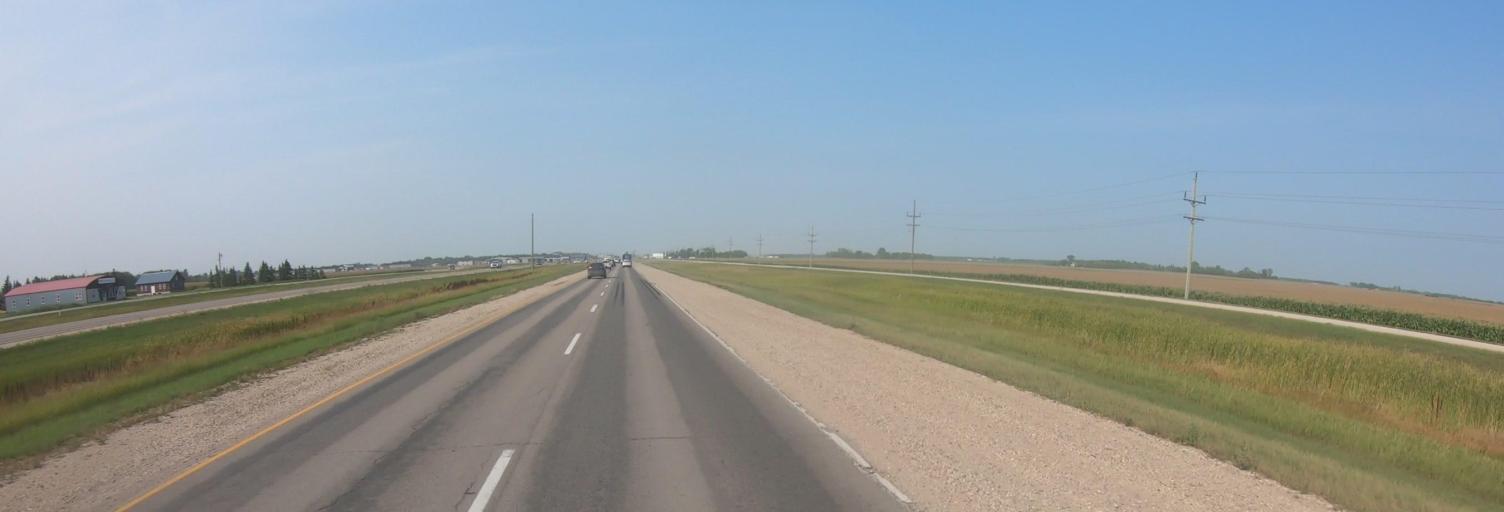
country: CA
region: Manitoba
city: Steinbach
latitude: 49.5863
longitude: -96.6875
